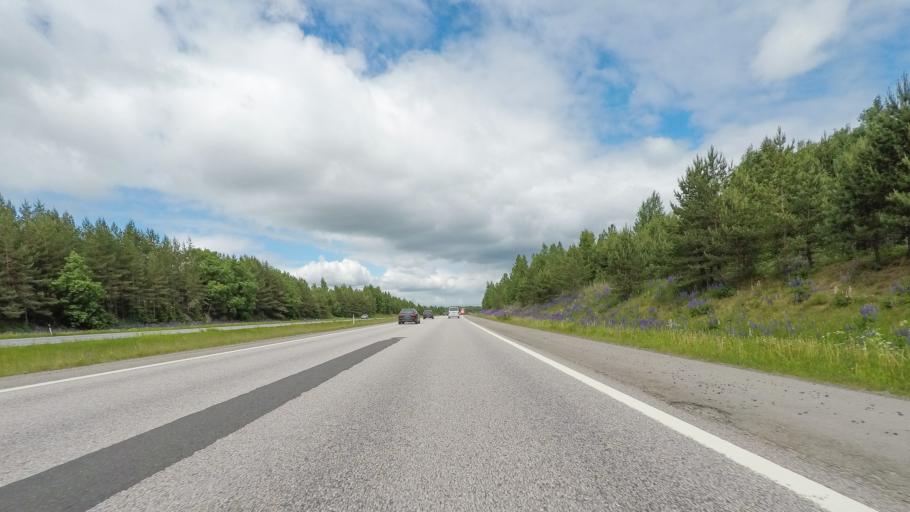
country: FI
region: Uusimaa
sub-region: Helsinki
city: Jaervenpaeae
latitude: 60.4846
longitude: 25.1379
